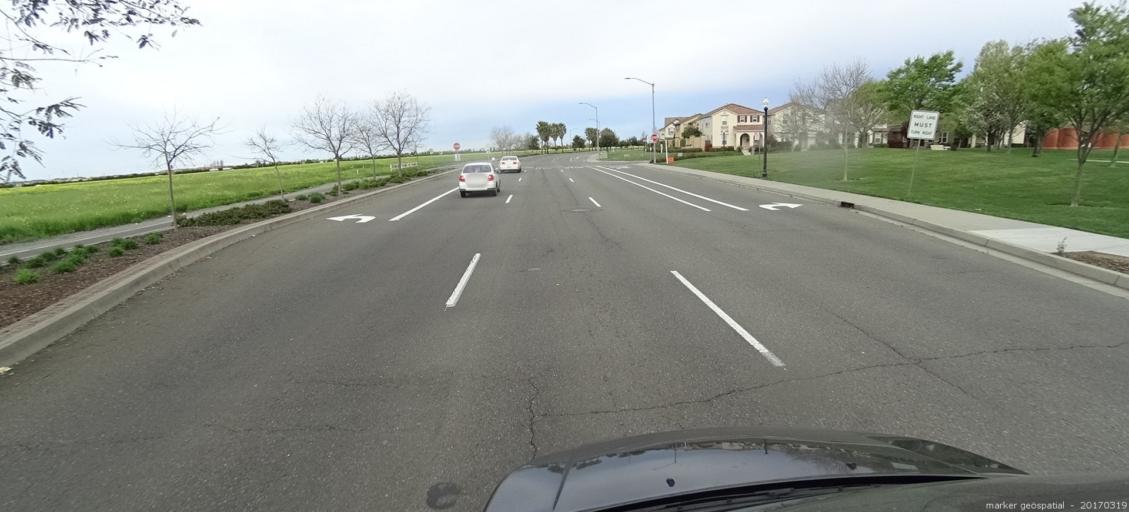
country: US
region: California
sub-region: Yolo County
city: West Sacramento
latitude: 38.6604
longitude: -121.5290
